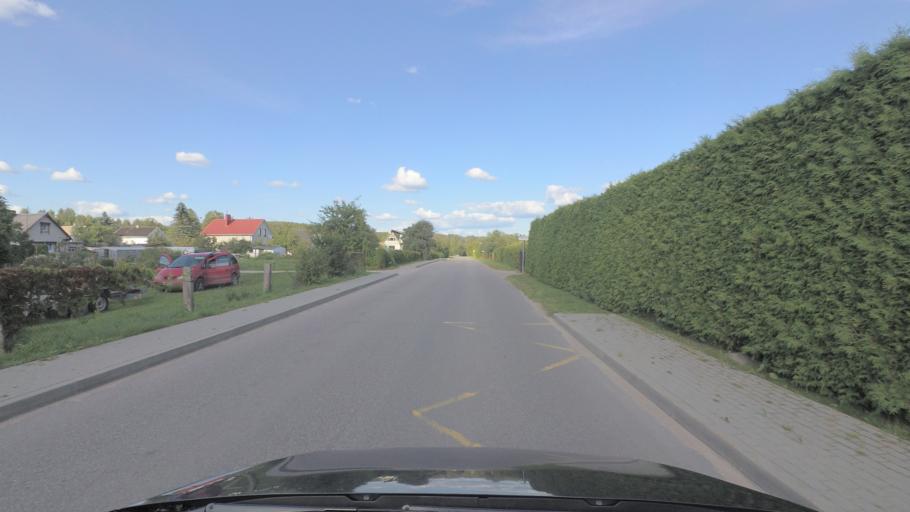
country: LT
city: Nemencine
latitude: 54.8571
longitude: 25.3837
